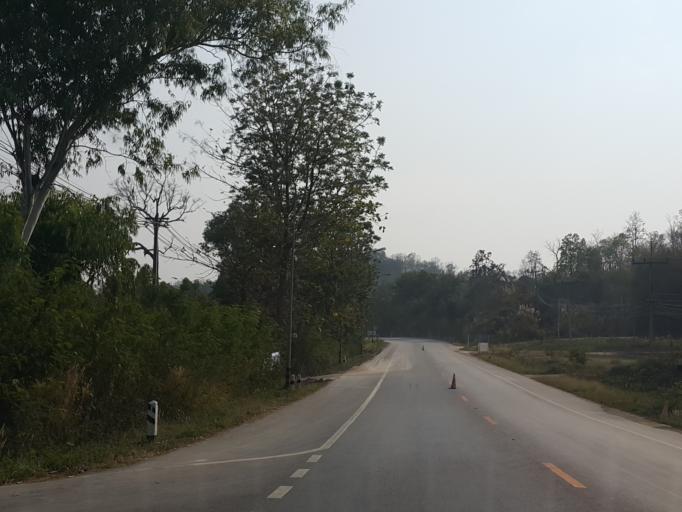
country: TH
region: Lampang
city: Chae Hom
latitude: 18.7108
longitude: 99.5569
